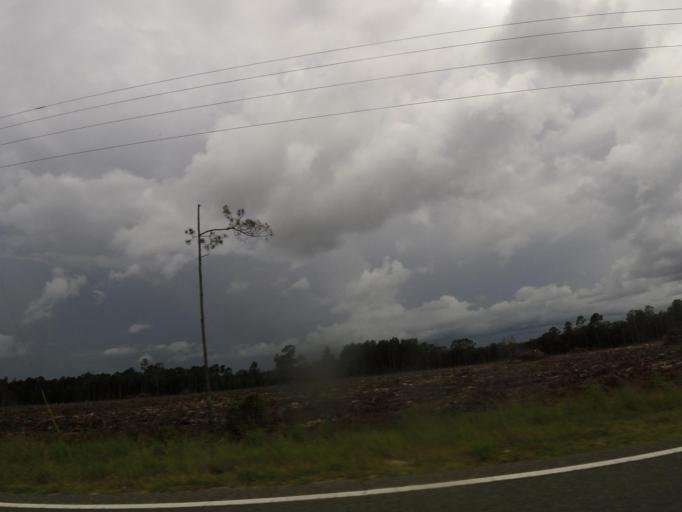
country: US
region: Florida
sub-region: Baker County
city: Macclenny
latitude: 30.5132
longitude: -82.2221
